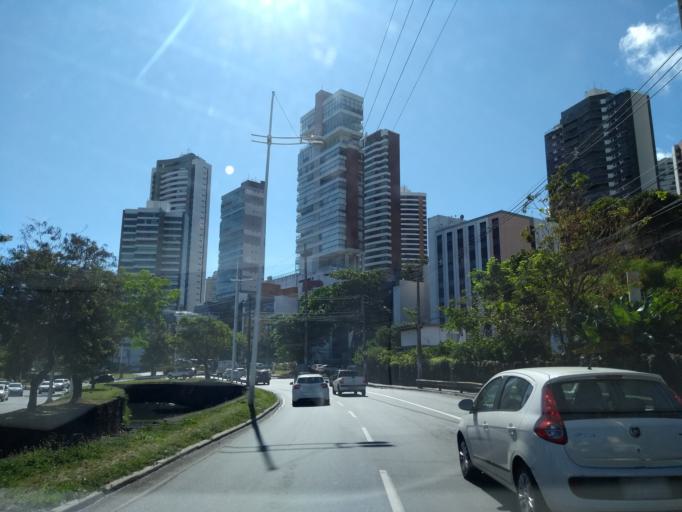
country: BR
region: Bahia
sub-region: Salvador
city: Salvador
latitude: -13.0062
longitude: -38.4890
